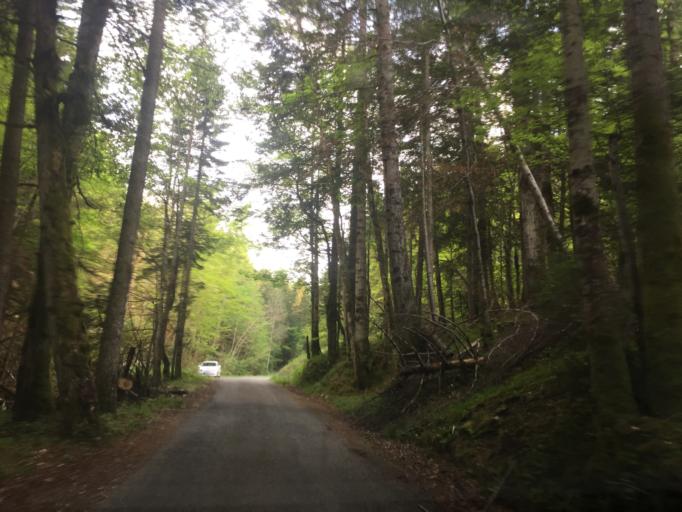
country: FR
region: Rhone-Alpes
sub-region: Departement de l'Isere
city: Le Sappey-en-Chartreuse
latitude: 45.2993
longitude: 5.8096
